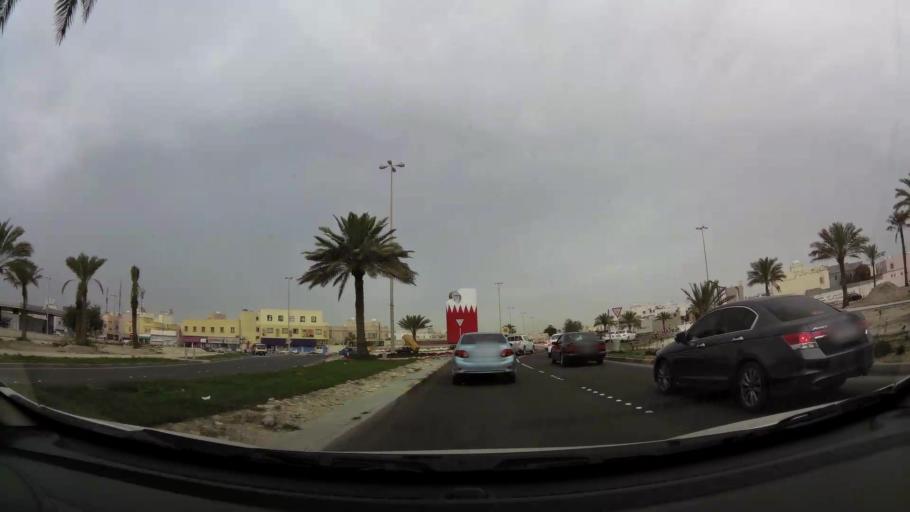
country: BH
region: Central Governorate
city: Dar Kulayb
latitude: 26.0621
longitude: 50.5080
